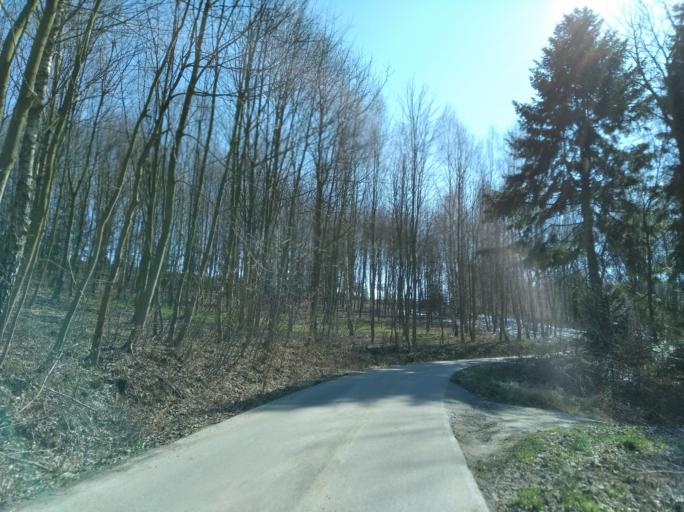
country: PL
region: Subcarpathian Voivodeship
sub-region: Powiat strzyzowski
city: Strzyzow
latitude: 49.8573
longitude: 21.8123
